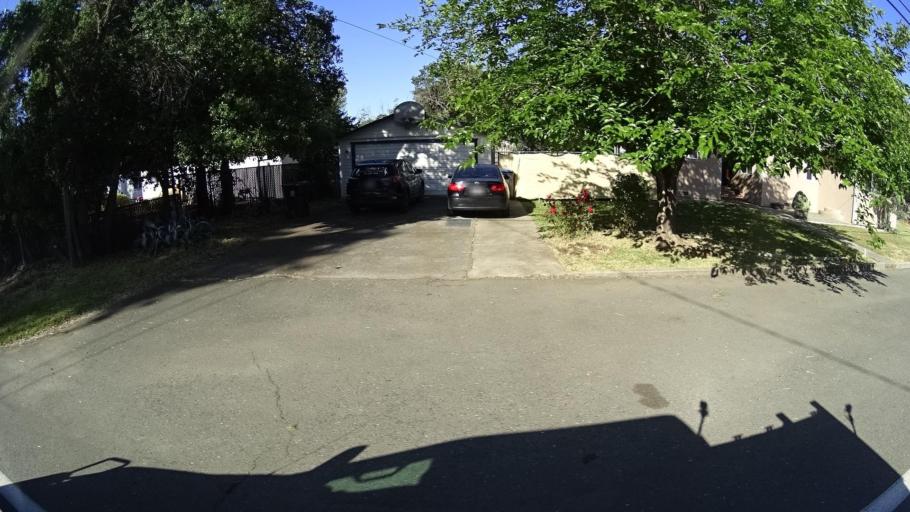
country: US
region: California
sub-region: Lake County
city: Lucerne
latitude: 39.0923
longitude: -122.7937
